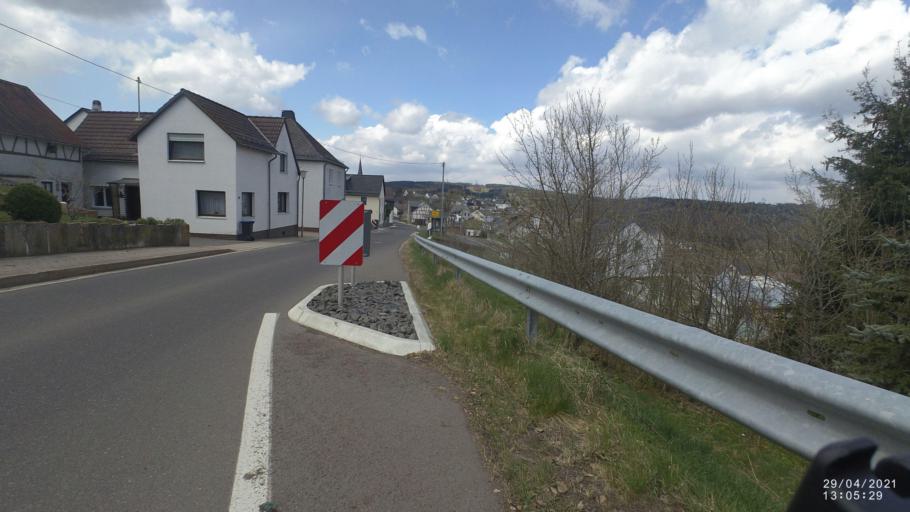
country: DE
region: Rheinland-Pfalz
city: Langenfeld
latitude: 50.3757
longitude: 7.0980
